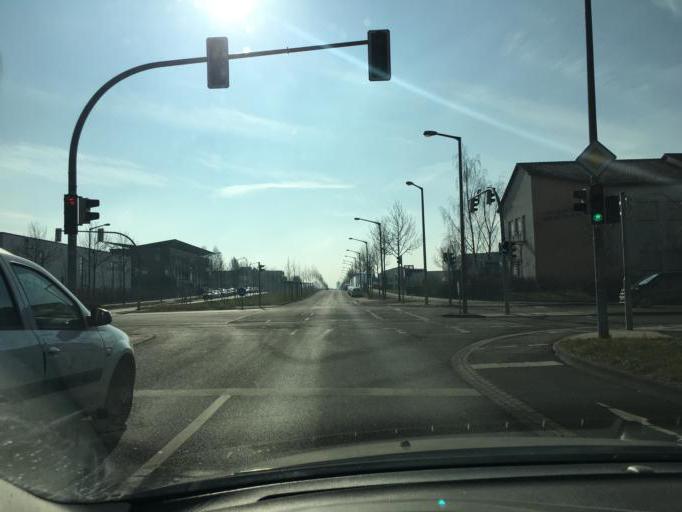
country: DE
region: Saxony
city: Taucha
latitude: 51.3692
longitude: 12.4305
